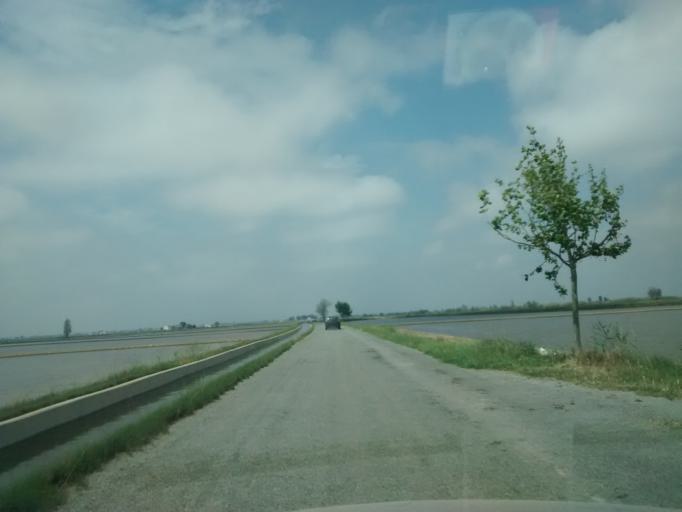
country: ES
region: Catalonia
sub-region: Provincia de Tarragona
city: Deltebre
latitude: 40.6883
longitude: 0.7826
